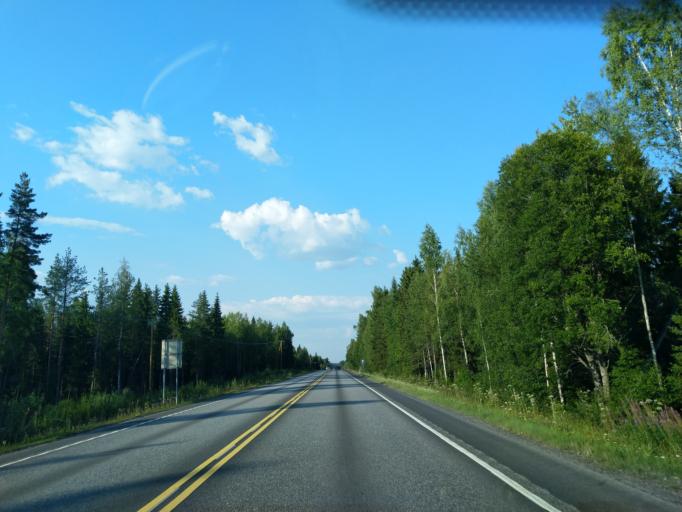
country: FI
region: Satakunta
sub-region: Pori
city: Pomarkku
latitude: 61.7222
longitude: 22.0564
